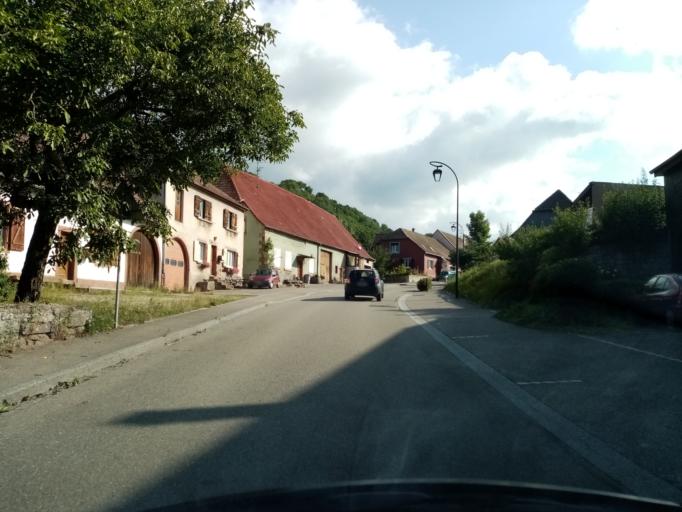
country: FR
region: Alsace
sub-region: Departement du Bas-Rhin
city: Ville
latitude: 48.3367
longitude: 7.3512
